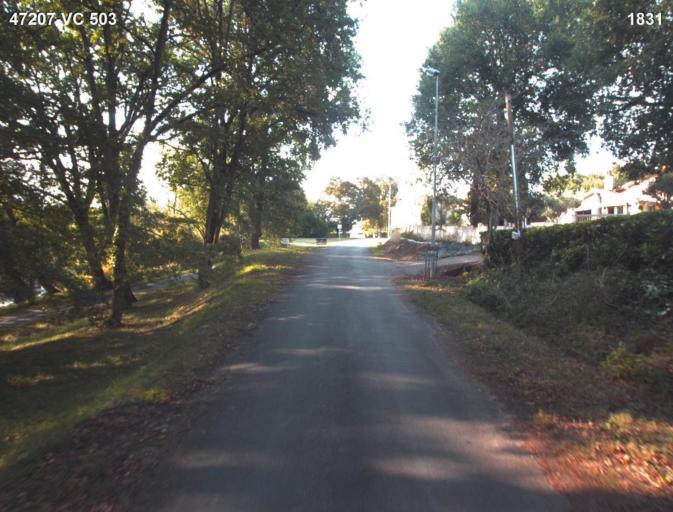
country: FR
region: Aquitaine
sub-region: Departement du Lot-et-Garonne
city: Barbaste
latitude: 44.1912
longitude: 0.2297
